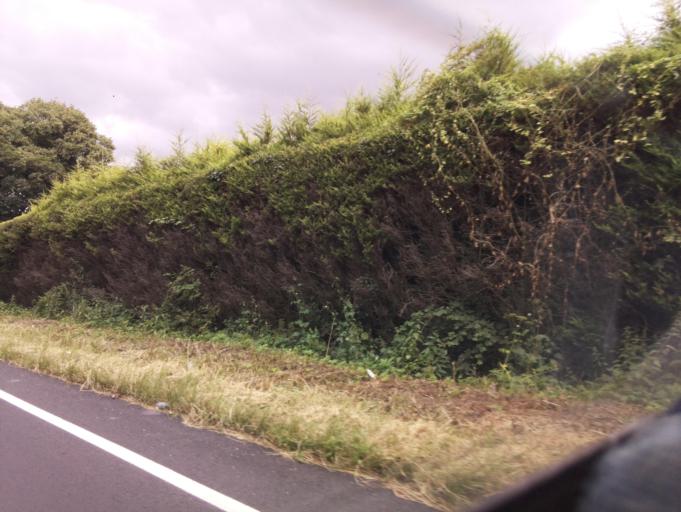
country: GB
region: England
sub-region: Nottinghamshire
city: Burton Joyce
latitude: 52.9945
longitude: -1.0249
